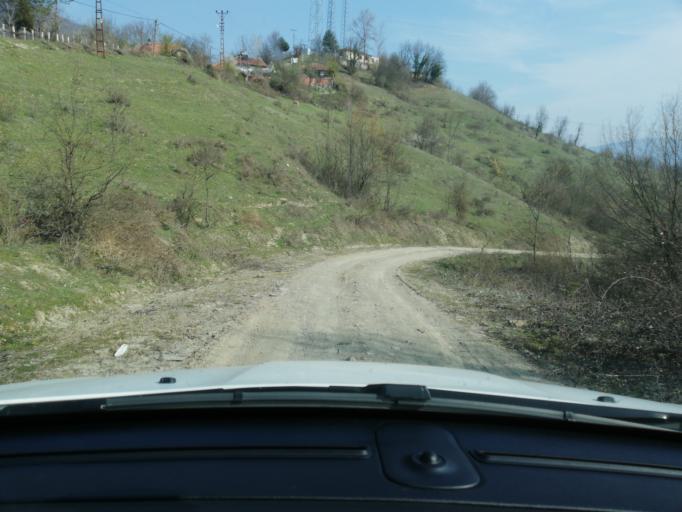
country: TR
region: Karabuk
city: Yenice
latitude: 41.2712
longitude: 32.3546
